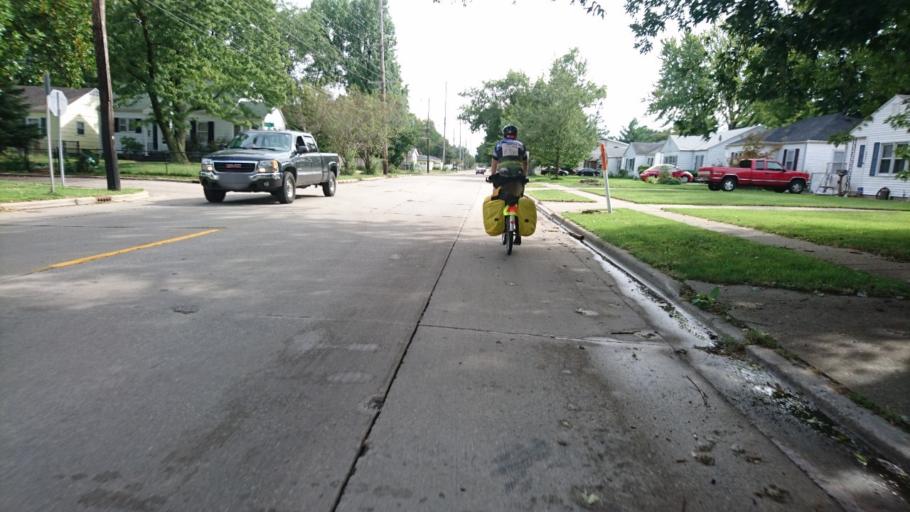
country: US
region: Illinois
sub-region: Sangamon County
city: Southern View
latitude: 39.7770
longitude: -89.6543
